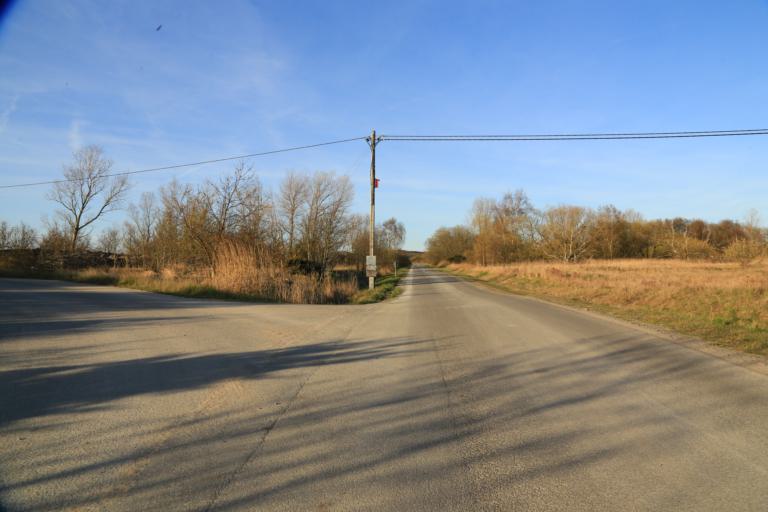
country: SE
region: Halland
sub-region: Varbergs Kommun
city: Varberg
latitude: 57.1257
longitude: 12.2546
